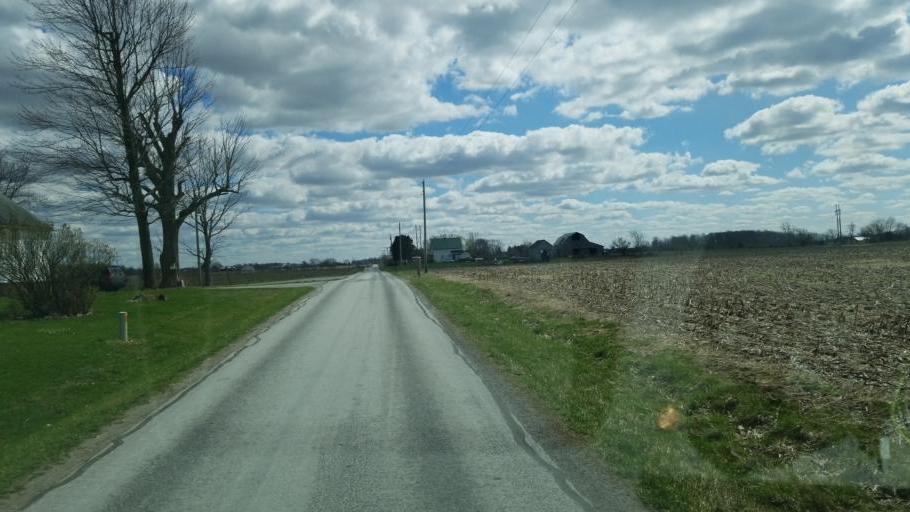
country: US
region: Ohio
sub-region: Hardin County
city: Kenton
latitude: 40.6190
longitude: -83.5596
